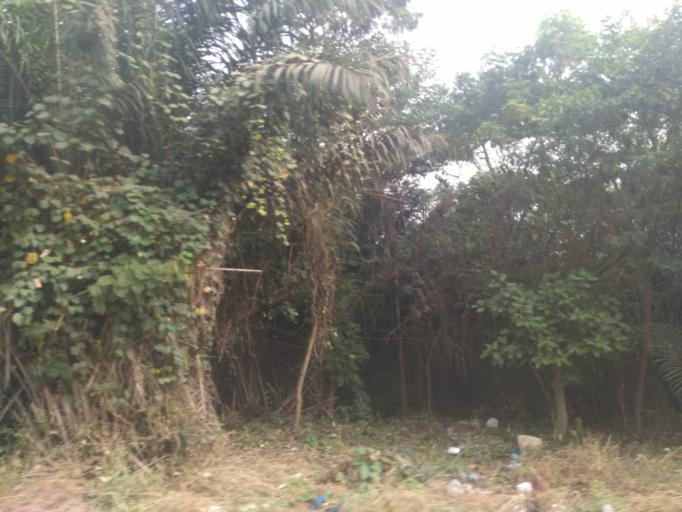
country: GH
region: Ashanti
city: Kumasi
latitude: 6.6658
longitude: -1.6138
